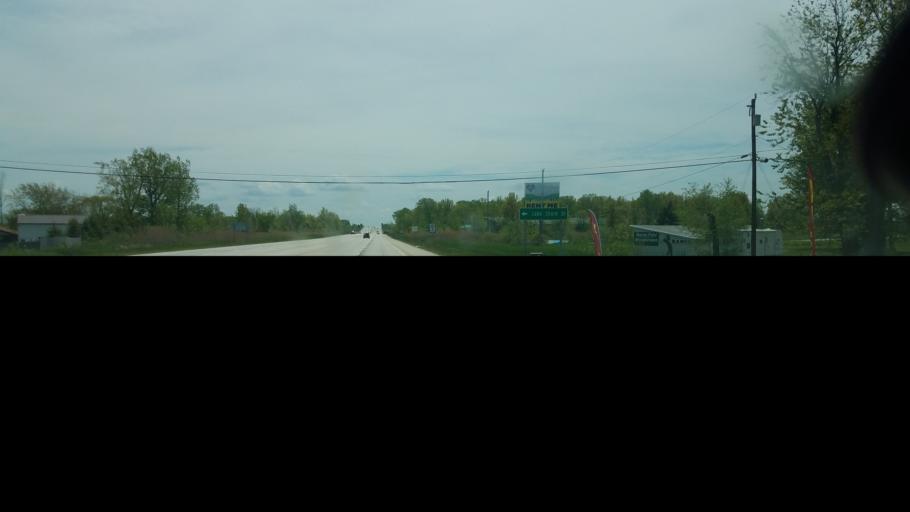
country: US
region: Ohio
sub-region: Ottawa County
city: Port Clinton
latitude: 41.5266
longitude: -83.0133
